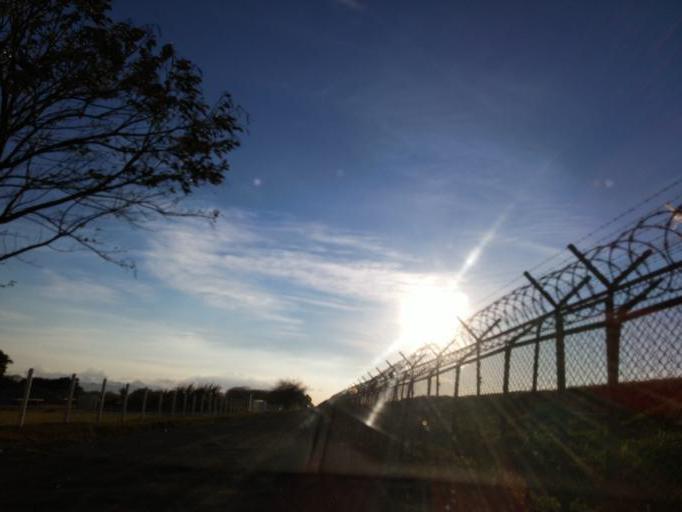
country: CR
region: Heredia
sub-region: Canton de Belen
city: San Antonio
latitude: 9.9951
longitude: -84.2026
